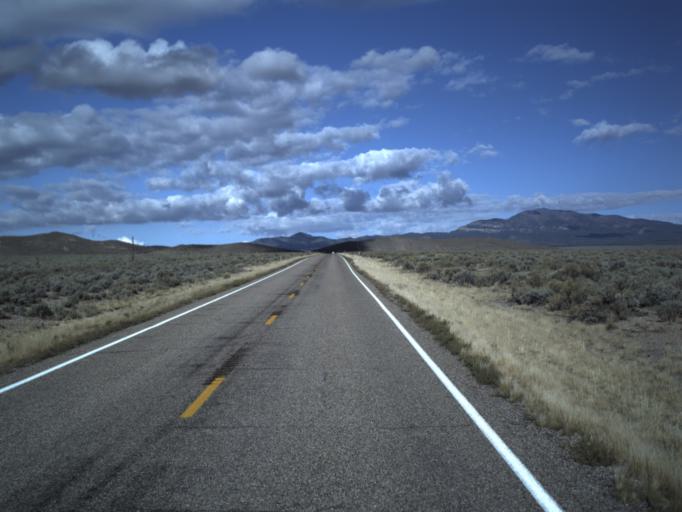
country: US
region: Utah
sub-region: Beaver County
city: Milford
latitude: 38.4180
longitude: -113.0900
